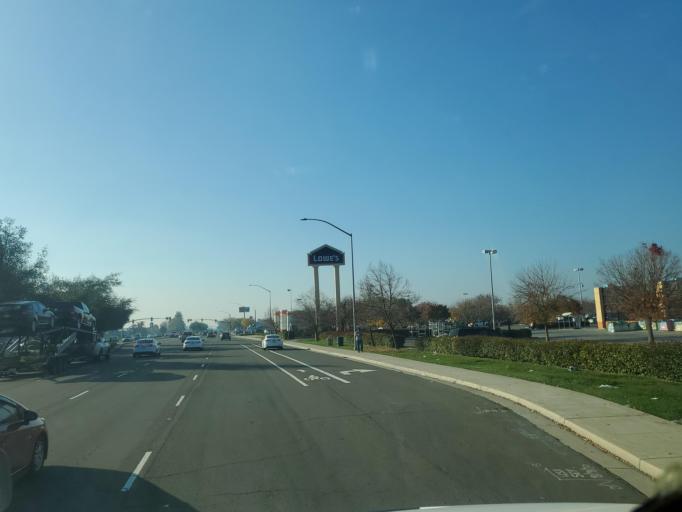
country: US
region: California
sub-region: San Joaquin County
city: Morada
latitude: 38.0213
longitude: -121.2691
